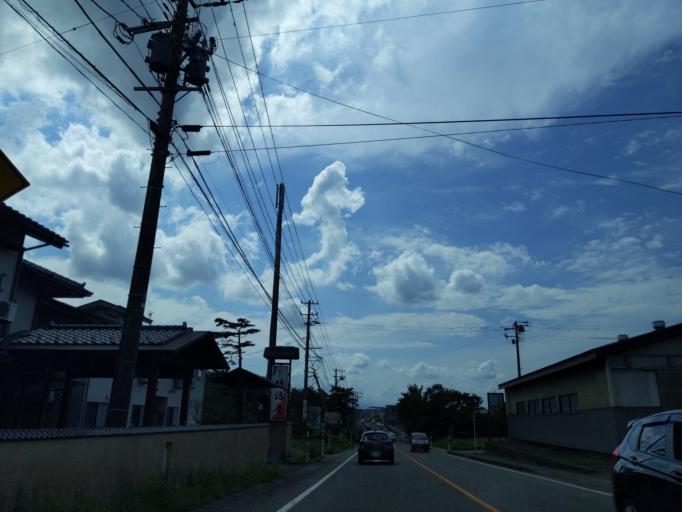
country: JP
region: Niigata
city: Joetsu
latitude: 37.2383
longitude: 138.3427
